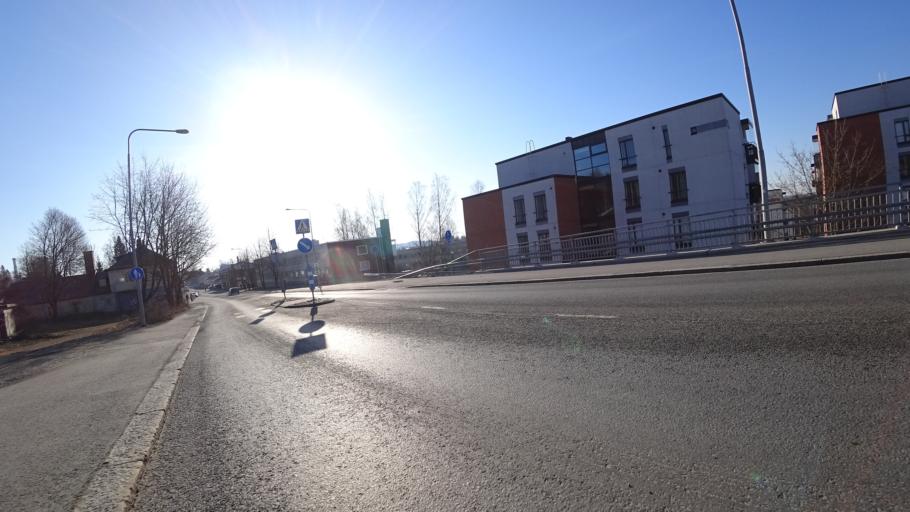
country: FI
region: Pirkanmaa
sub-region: Tampere
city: Pirkkala
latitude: 61.5074
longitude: 23.6633
